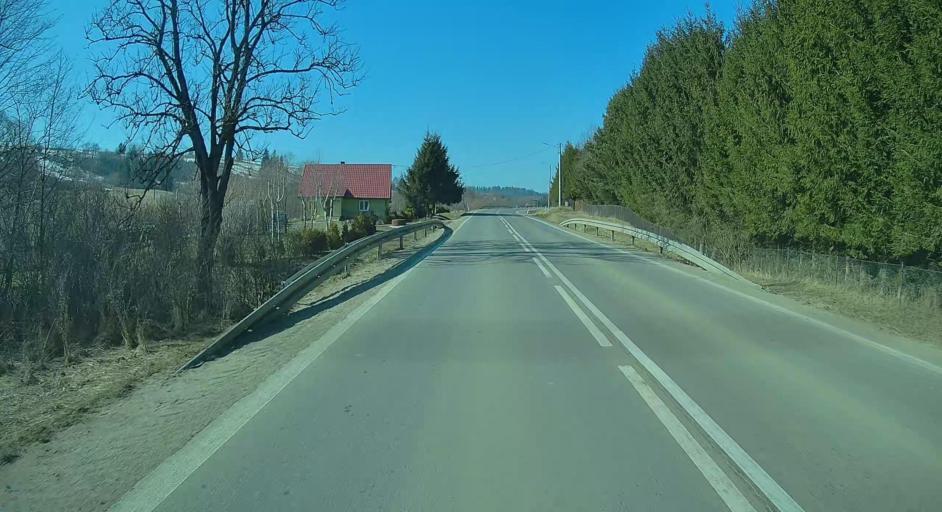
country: PL
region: Subcarpathian Voivodeship
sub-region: Powiat bieszczadzki
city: Ustrzyki Dolne
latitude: 49.5012
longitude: 22.6285
